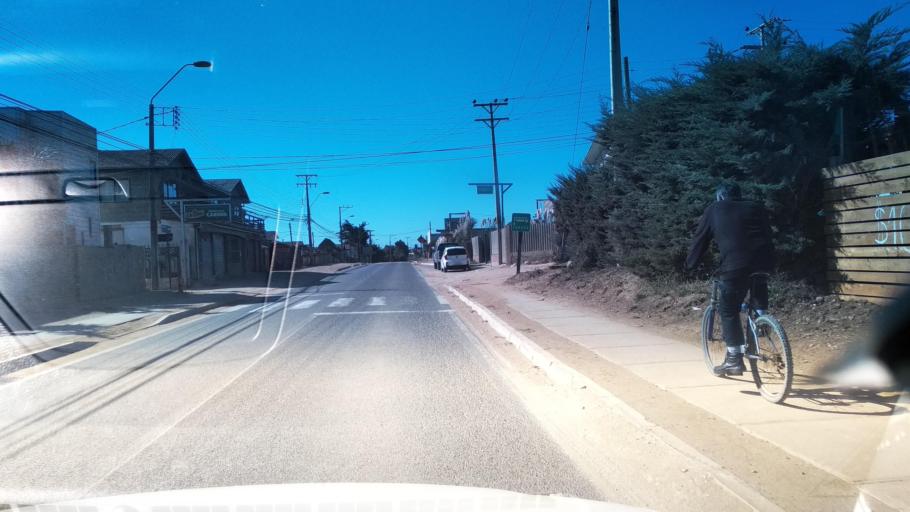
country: CL
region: O'Higgins
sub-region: Provincia de Colchagua
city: Santa Cruz
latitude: -34.4019
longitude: -72.0241
